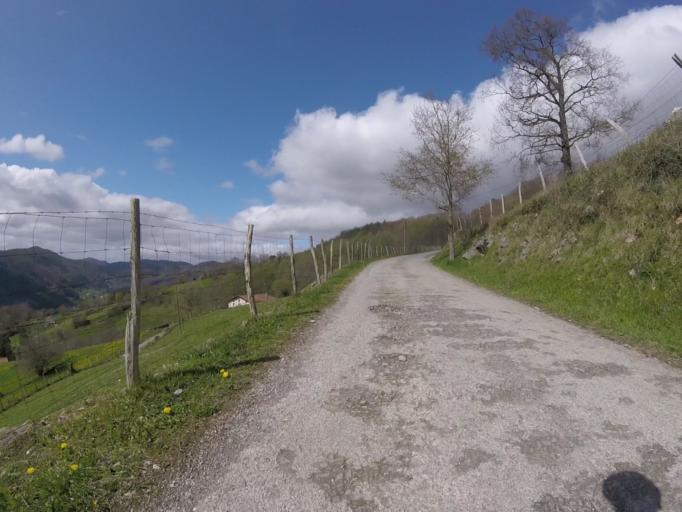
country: ES
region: Basque Country
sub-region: Provincia de Guipuzcoa
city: Albiztur
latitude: 43.1388
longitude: -2.1136
